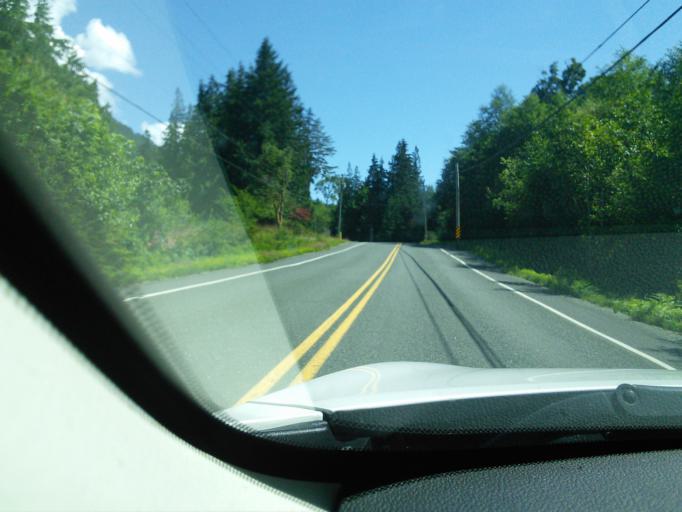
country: CA
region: British Columbia
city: Campbell River
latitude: 50.3526
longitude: -125.9079
